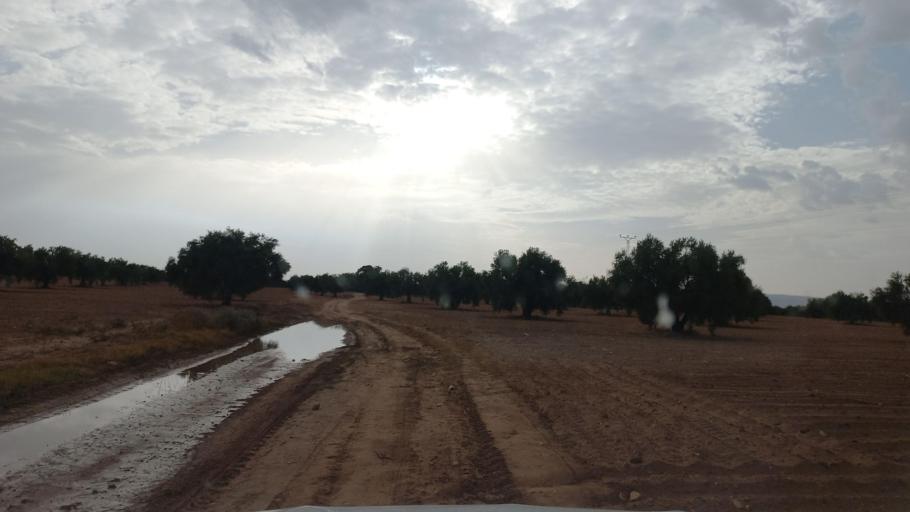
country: TN
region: Al Qasrayn
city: Sbiba
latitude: 35.2948
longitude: 9.0698
